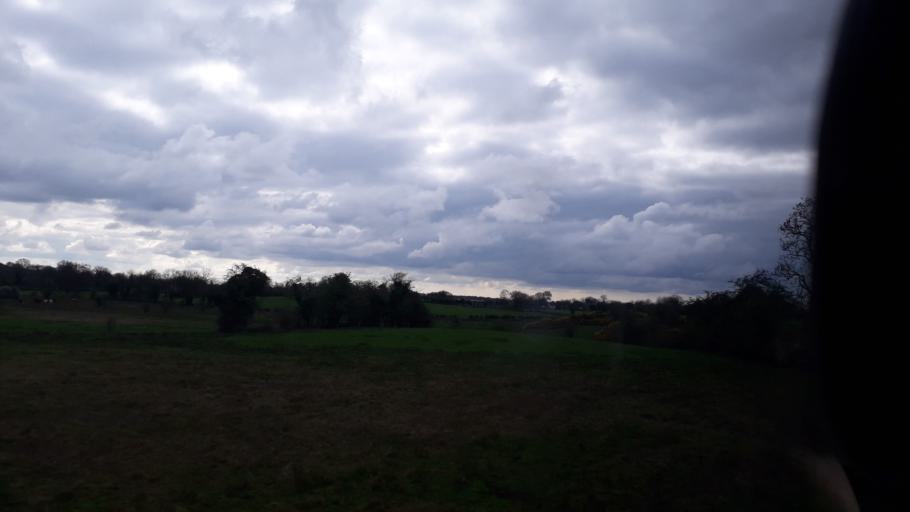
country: IE
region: Leinster
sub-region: An Longfort
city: Edgeworthstown
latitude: 53.7025
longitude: -7.6970
